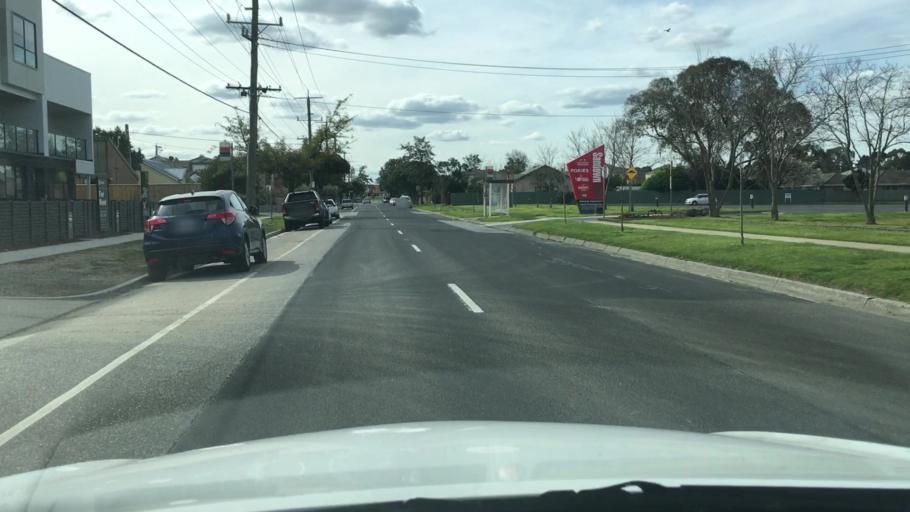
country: AU
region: Victoria
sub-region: Greater Dandenong
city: Springvale
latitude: -37.9569
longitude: 145.1575
